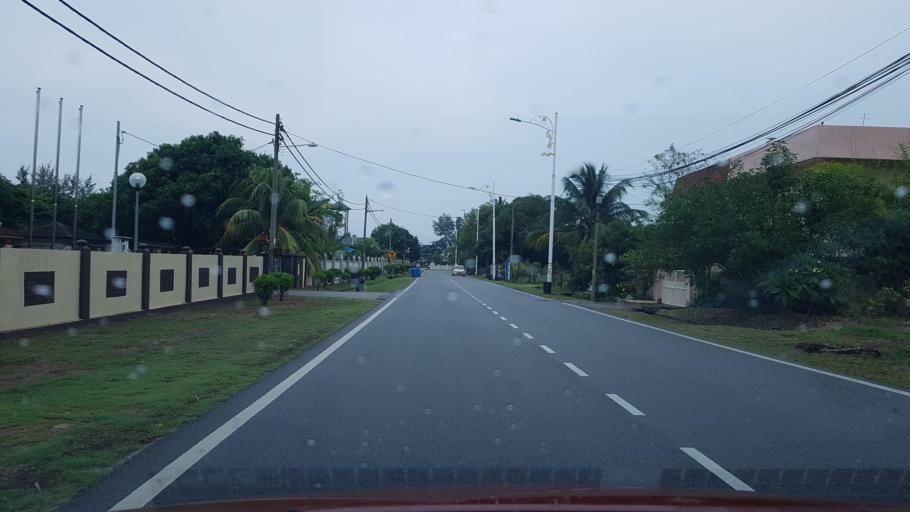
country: MY
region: Terengganu
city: Kuala Terengganu
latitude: 5.3163
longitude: 103.1552
